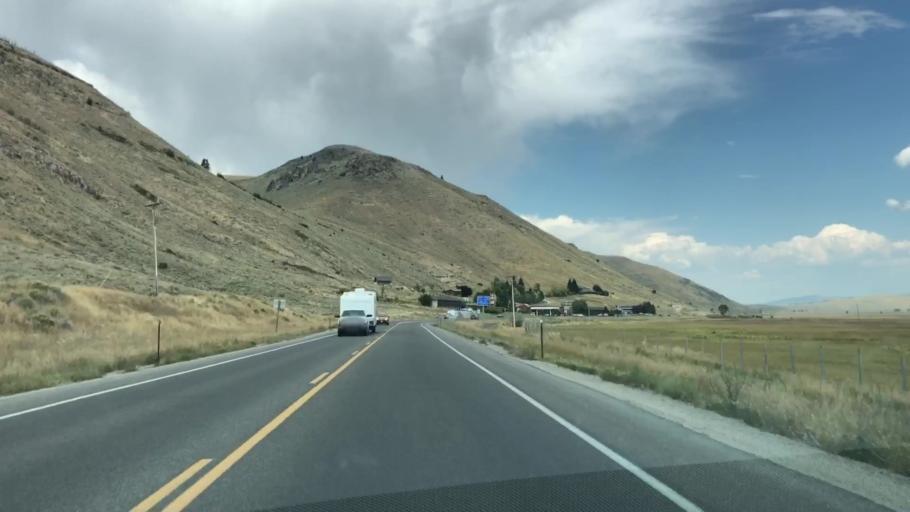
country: US
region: Wyoming
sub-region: Teton County
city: Jackson
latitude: 43.5014
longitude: -110.7589
